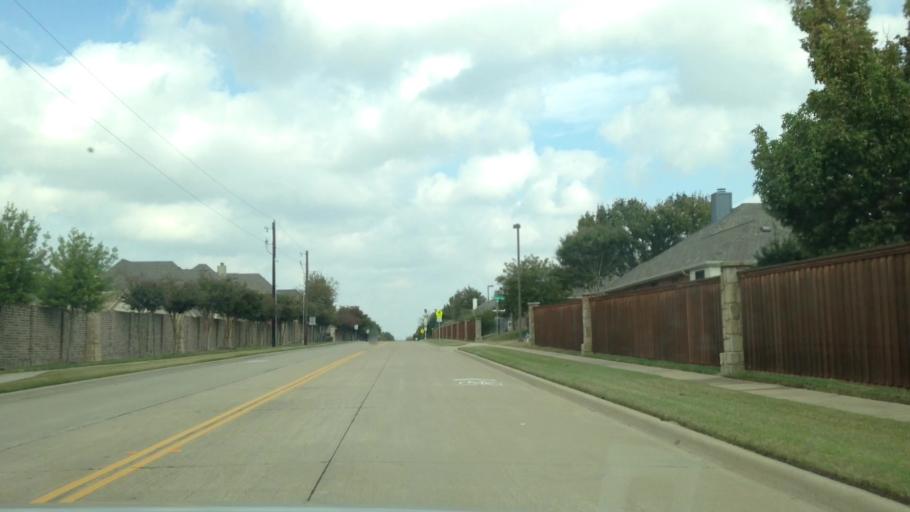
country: US
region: Texas
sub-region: Collin County
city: Allen
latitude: 33.1185
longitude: -96.7070
